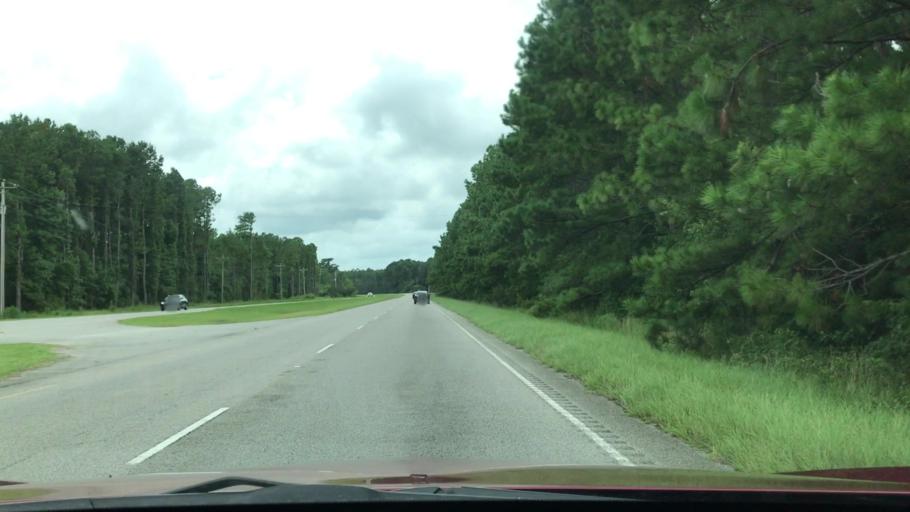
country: US
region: South Carolina
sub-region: Charleston County
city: Awendaw
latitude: 33.0382
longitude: -79.6096
